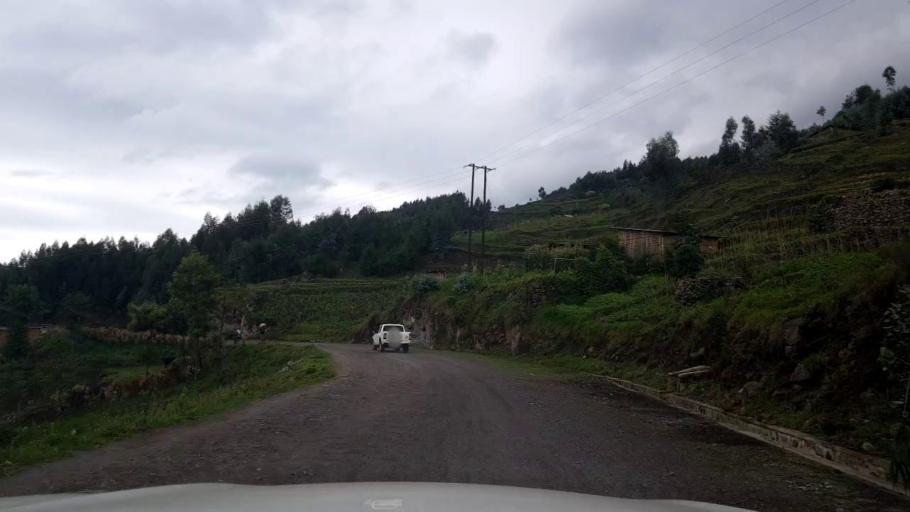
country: RW
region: Northern Province
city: Musanze
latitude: -1.4910
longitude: 29.5310
